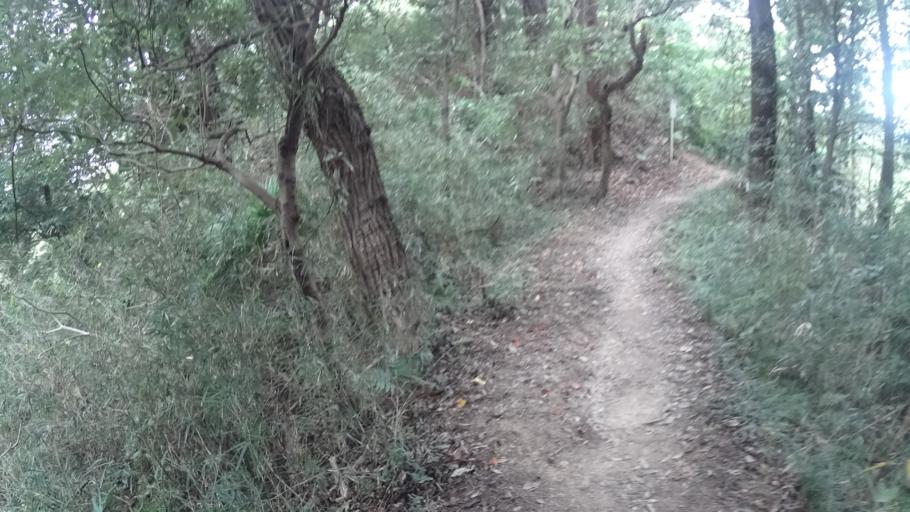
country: JP
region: Kanagawa
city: Zushi
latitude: 35.2933
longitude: 139.6027
